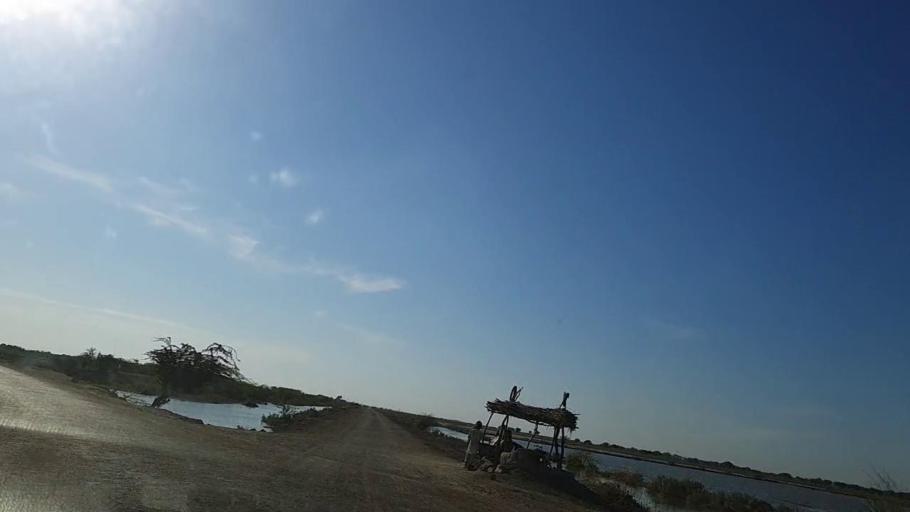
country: PK
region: Sindh
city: Pithoro
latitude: 25.5088
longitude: 69.4469
